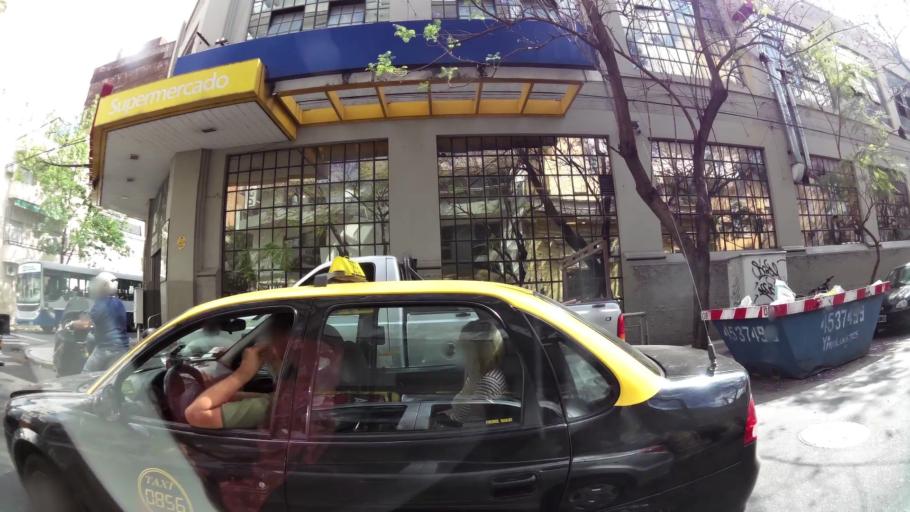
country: AR
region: Santa Fe
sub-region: Departamento de Rosario
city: Rosario
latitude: -32.9513
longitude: -60.6479
